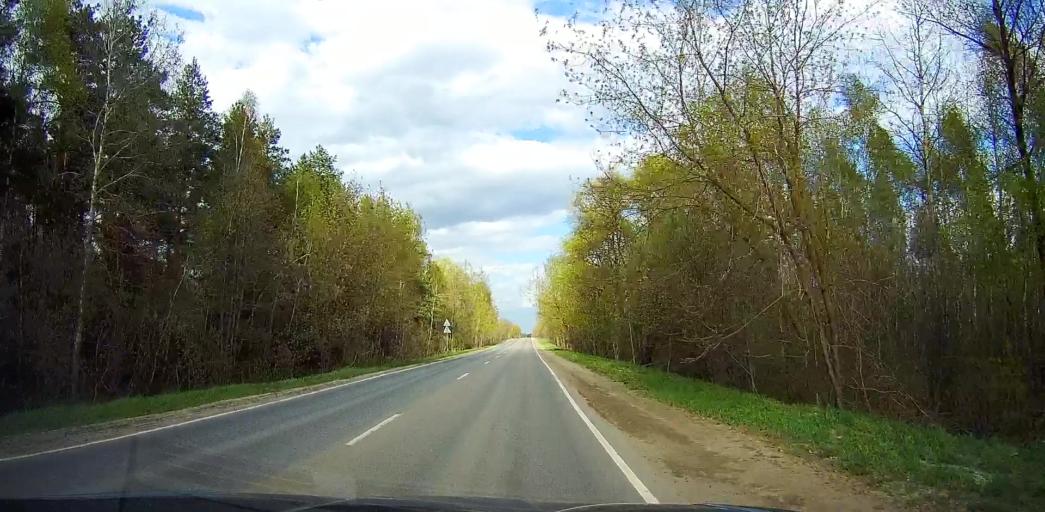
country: RU
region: Moskovskaya
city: Rakhmanovo
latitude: 55.7363
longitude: 38.6360
